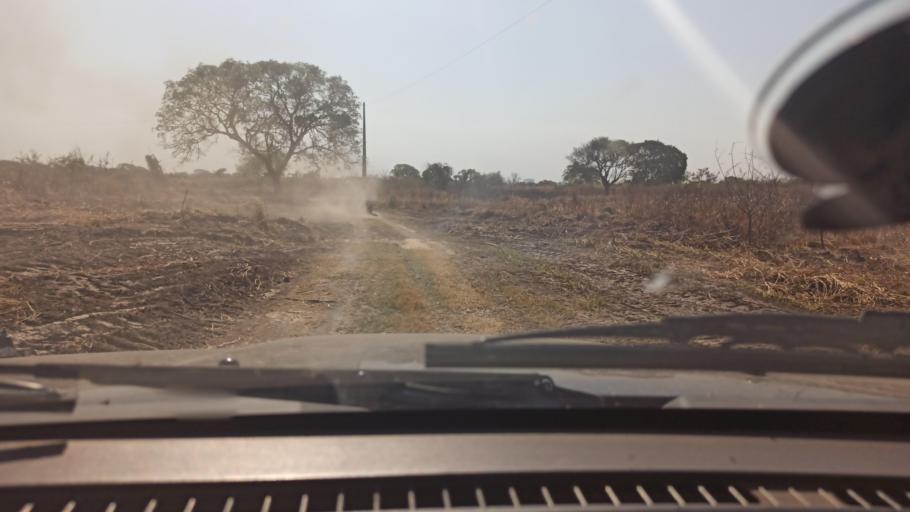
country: PY
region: Asuncion
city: Asuncion
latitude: -25.3436
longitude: -57.6757
